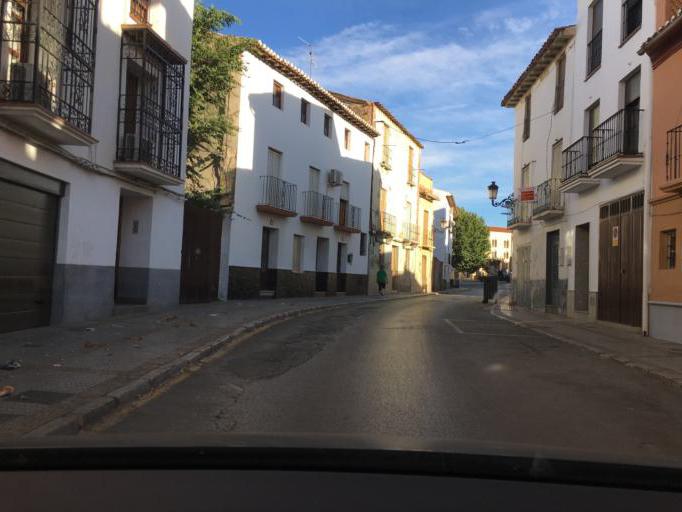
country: ES
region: Andalusia
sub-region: Provincia de Granada
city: Guadix
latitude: 37.2976
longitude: -3.1349
